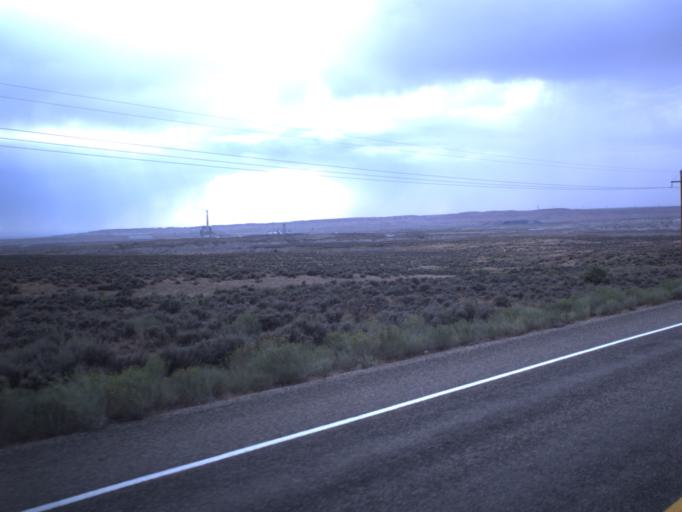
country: US
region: Colorado
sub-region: Rio Blanco County
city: Rangely
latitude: 40.0794
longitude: -109.2115
